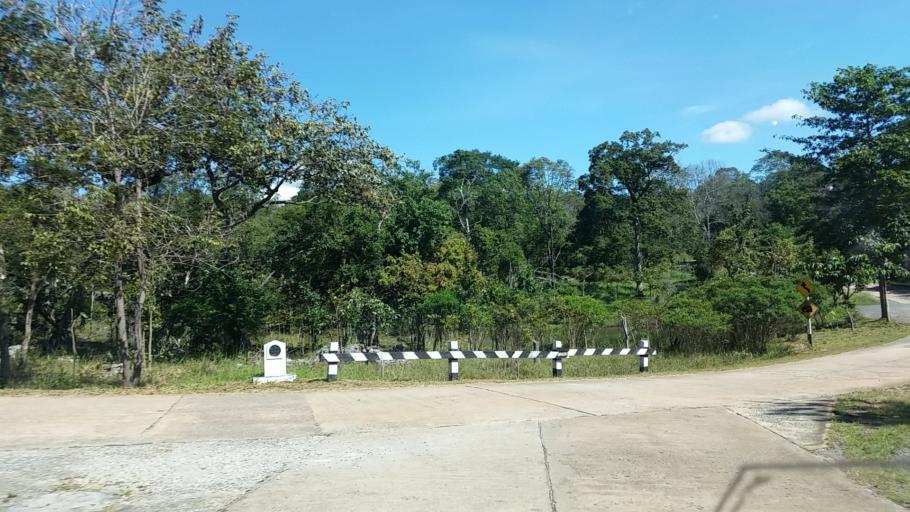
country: TH
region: Chaiyaphum
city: Sap Yai
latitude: 15.6357
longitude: 101.3922
